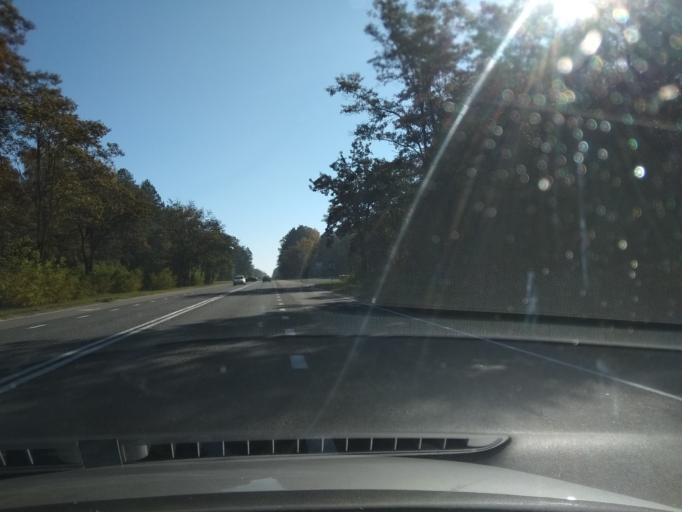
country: BY
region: Brest
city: Malaryta
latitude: 51.9228
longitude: 24.0782
